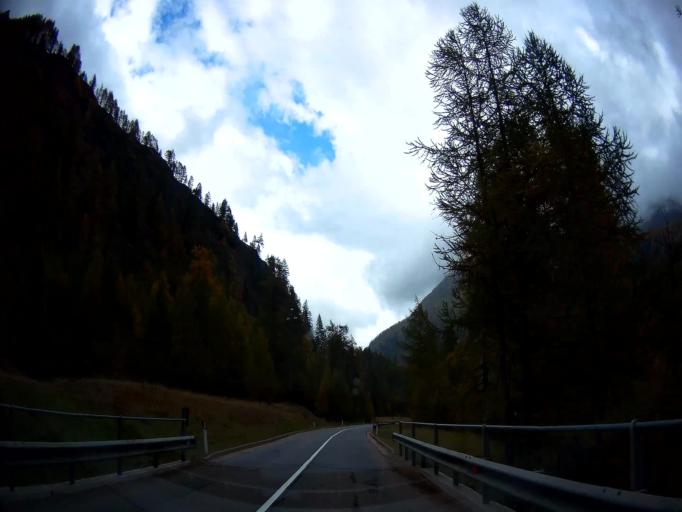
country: IT
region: Trentino-Alto Adige
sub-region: Bolzano
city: Senales
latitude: 46.7333
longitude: 10.8080
